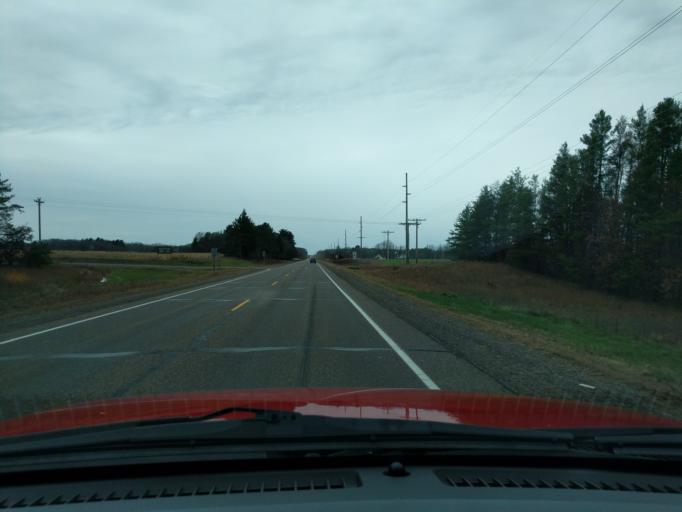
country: US
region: Wisconsin
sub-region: Washburn County
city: Shell Lake
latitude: 45.8151
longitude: -92.0056
